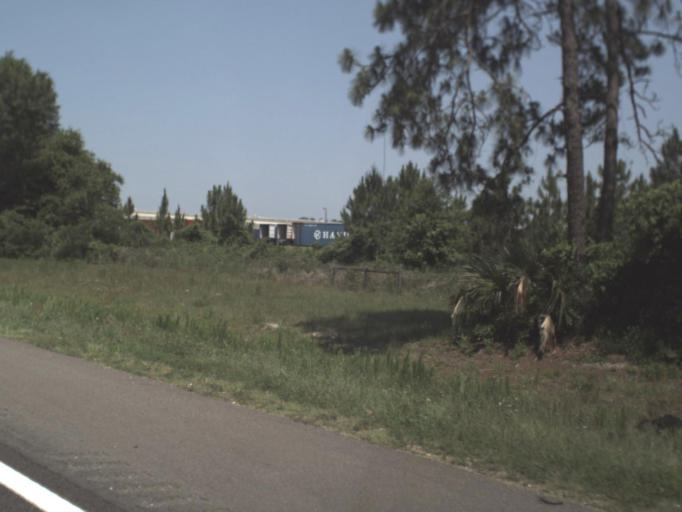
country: US
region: Florida
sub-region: Duval County
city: Jacksonville
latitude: 30.3146
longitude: -81.8024
